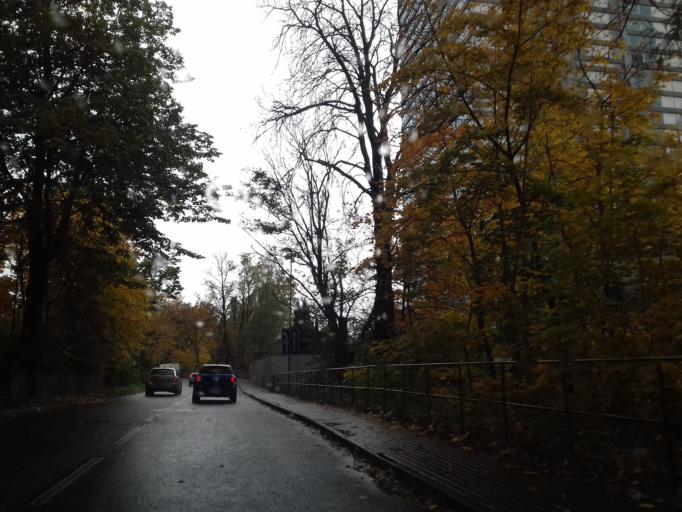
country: CZ
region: Liberecky
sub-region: Okres Liberec
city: Liberec
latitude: 50.7635
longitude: 15.0545
